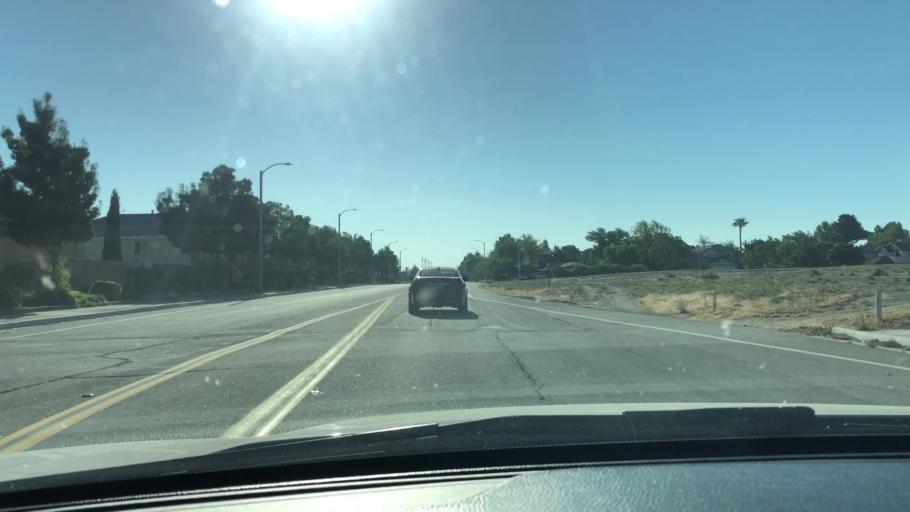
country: US
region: California
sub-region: Los Angeles County
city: Quartz Hill
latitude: 34.6676
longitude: -118.1782
